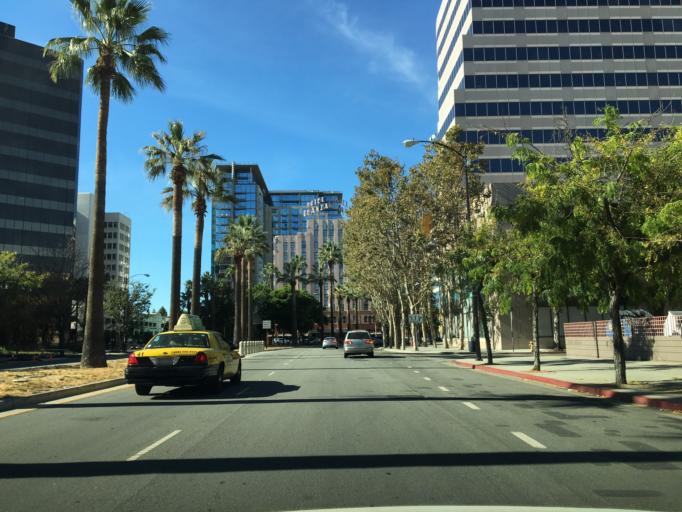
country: US
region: California
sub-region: Santa Clara County
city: San Jose
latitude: 37.3329
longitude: -121.8940
